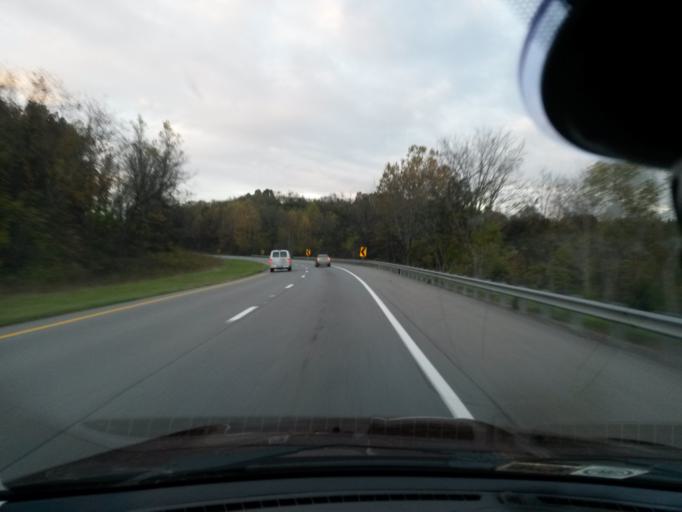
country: US
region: Virginia
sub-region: Botetourt County
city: Fincastle
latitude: 37.6025
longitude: -79.8374
